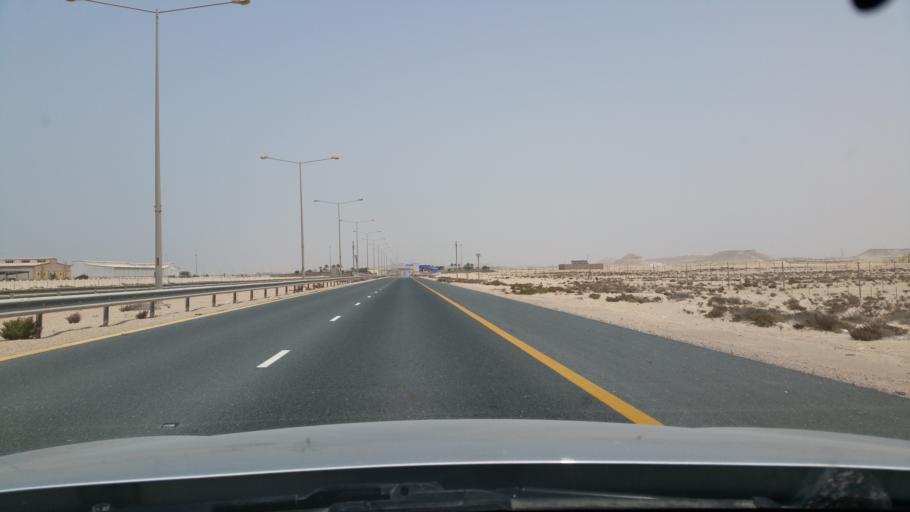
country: QA
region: Baladiyat ar Rayyan
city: Dukhan
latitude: 25.3796
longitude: 50.7816
